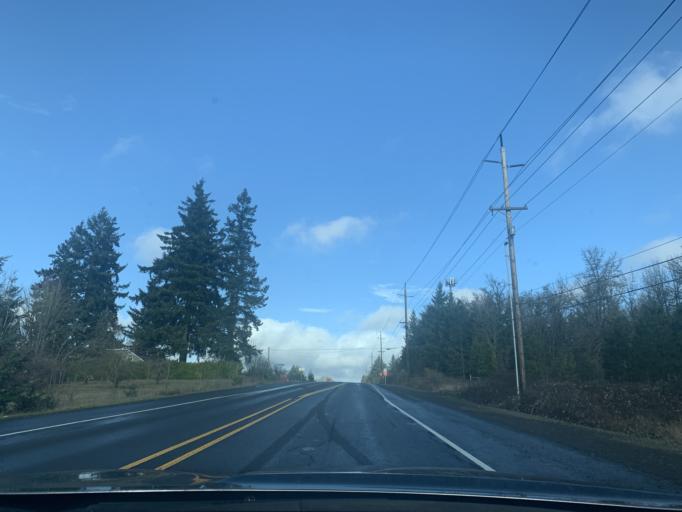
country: US
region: Oregon
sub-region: Washington County
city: Sherwood
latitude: 45.4022
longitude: -122.8517
